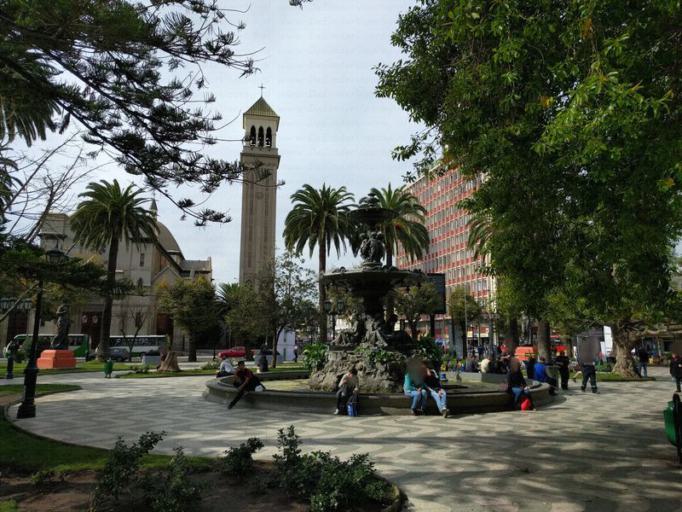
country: CL
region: Valparaiso
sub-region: Provincia de Valparaiso
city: Valparaiso
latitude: -33.0462
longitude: -71.6200
